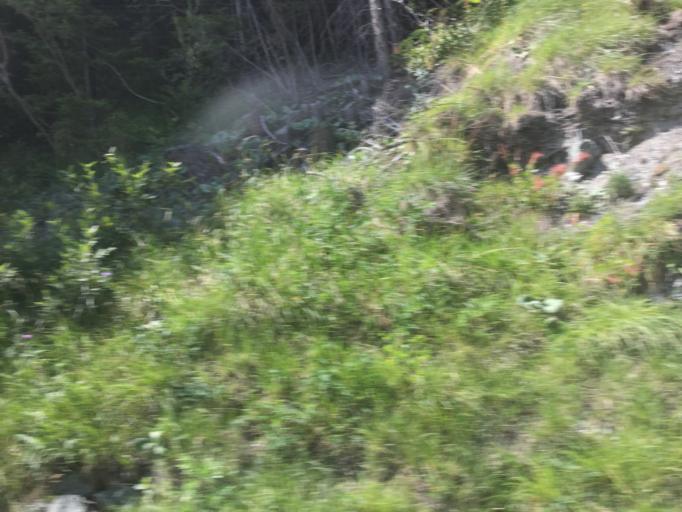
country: CH
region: Grisons
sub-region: Maloja District
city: Silvaplana
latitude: 46.4848
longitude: 9.6409
